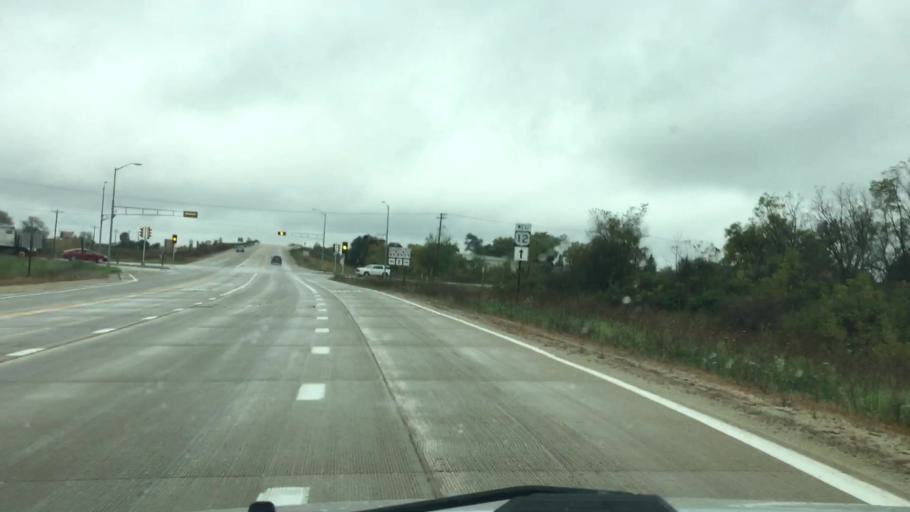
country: US
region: Wisconsin
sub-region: Walworth County
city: Whitewater
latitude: 42.8202
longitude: -88.7437
